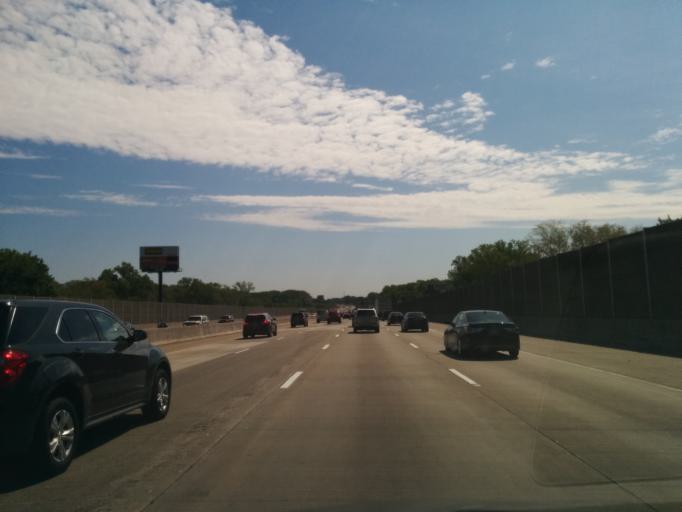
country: US
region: Indiana
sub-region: Lake County
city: New Chicago
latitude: 41.5733
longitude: -87.2780
